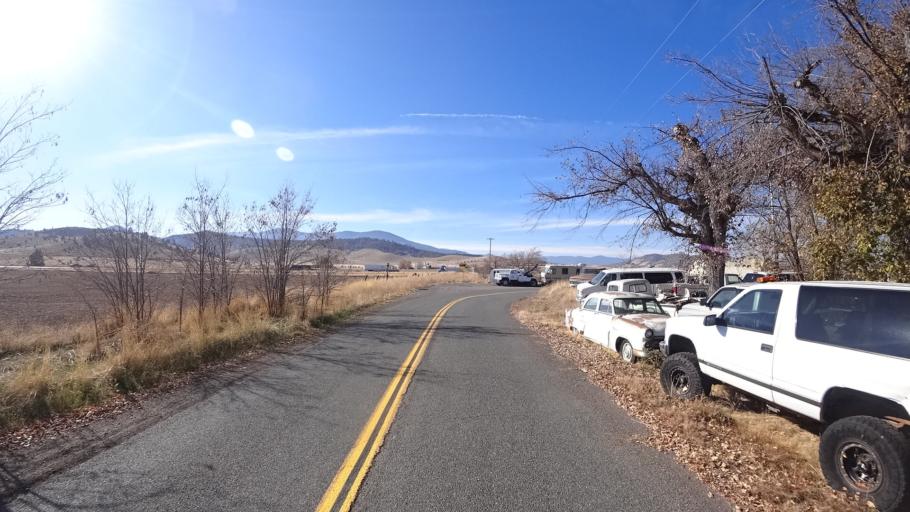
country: US
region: California
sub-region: Siskiyou County
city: Montague
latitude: 41.6456
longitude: -122.5315
